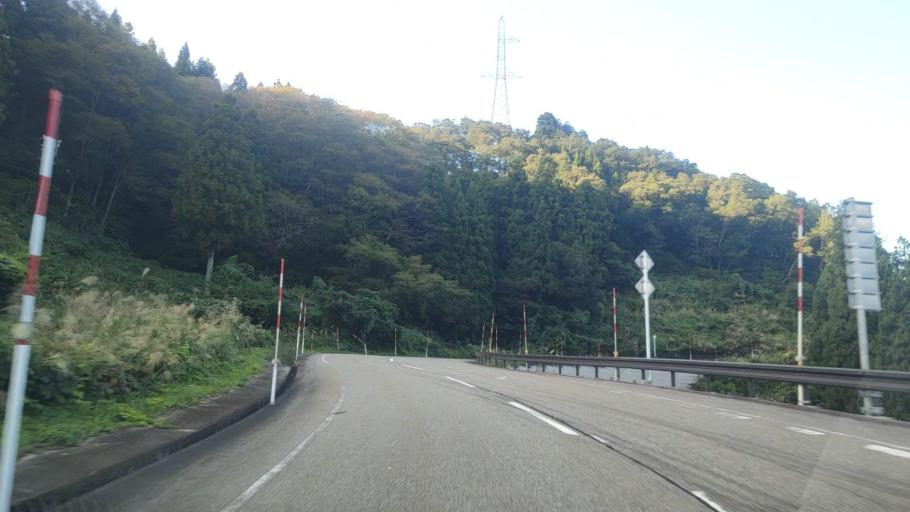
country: JP
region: Toyama
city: Yatsuomachi-higashikumisaka
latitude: 36.5055
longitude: 137.0618
